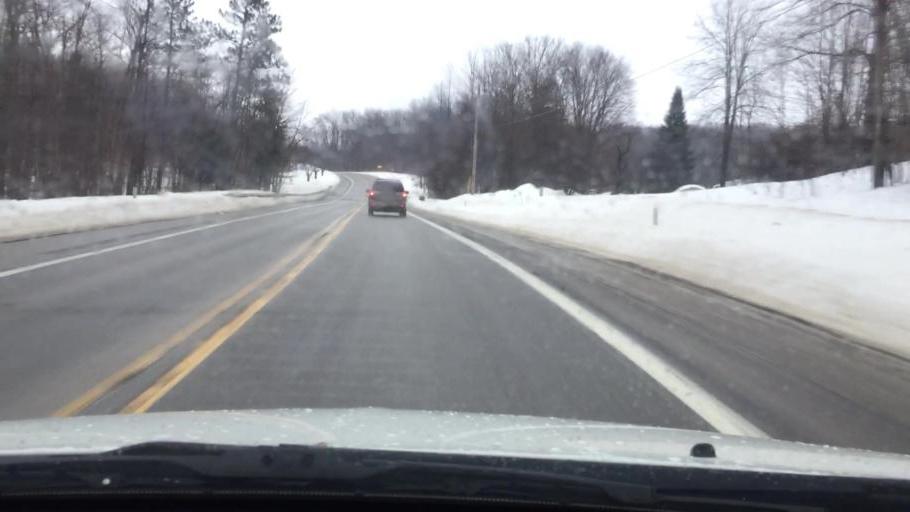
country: US
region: Michigan
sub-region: Charlevoix County
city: East Jordan
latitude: 45.2134
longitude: -85.1718
